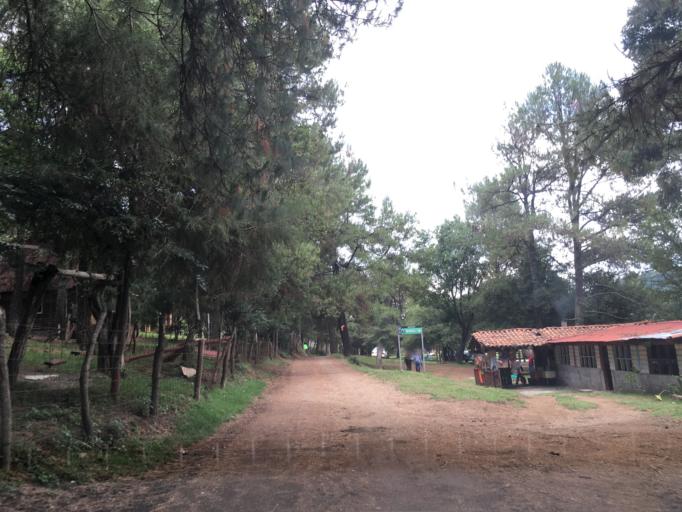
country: MX
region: Michoacan
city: Acuitzio del Canje
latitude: 19.5247
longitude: -101.2451
